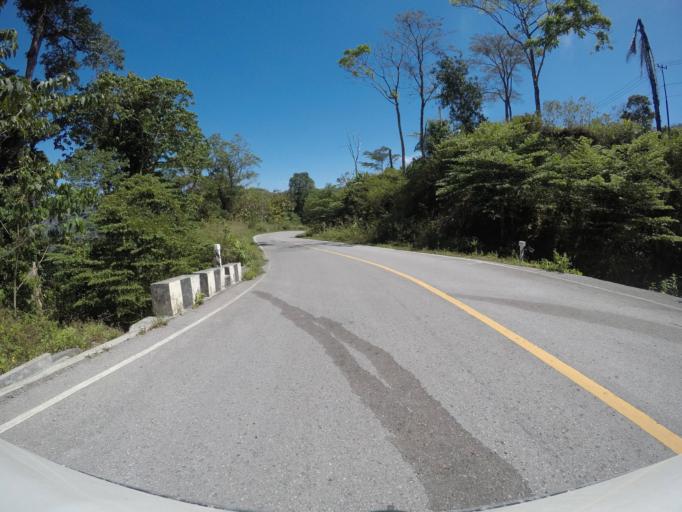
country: TL
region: Manatuto
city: Manatuto
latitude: -8.8242
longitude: 125.9798
